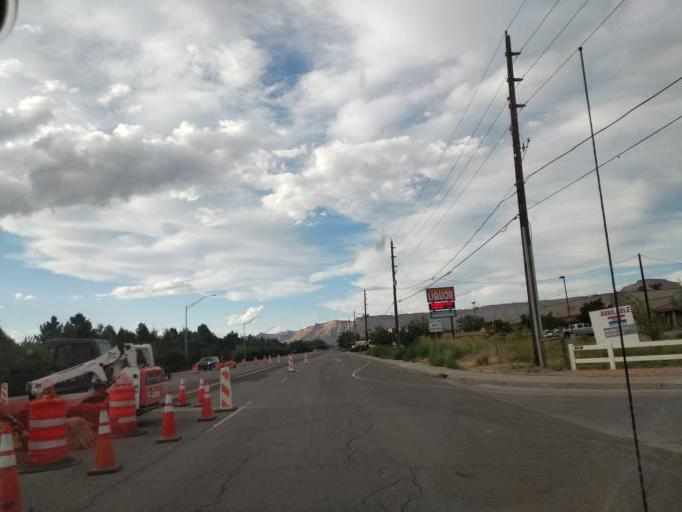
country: US
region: Colorado
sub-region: Mesa County
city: Clifton
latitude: 39.0640
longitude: -108.4593
